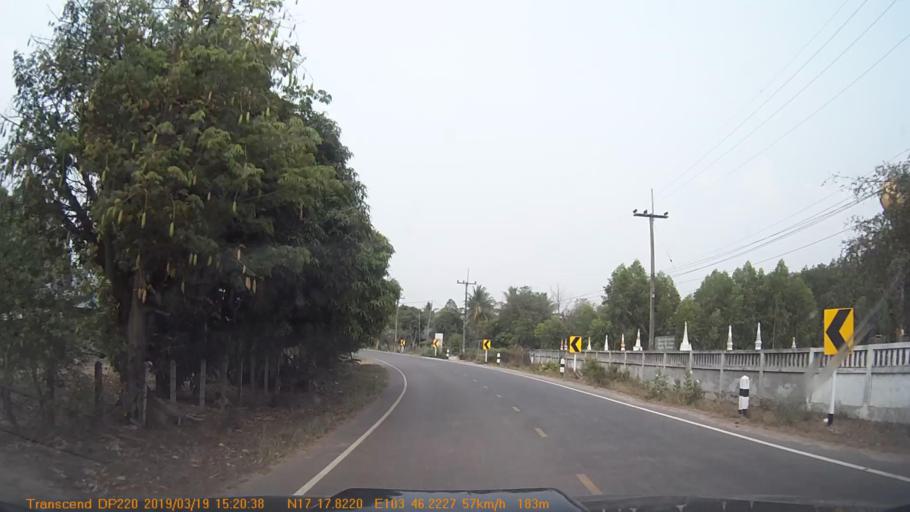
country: TH
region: Sakon Nakhon
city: Phanna Nikhom
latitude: 17.2973
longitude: 103.7706
